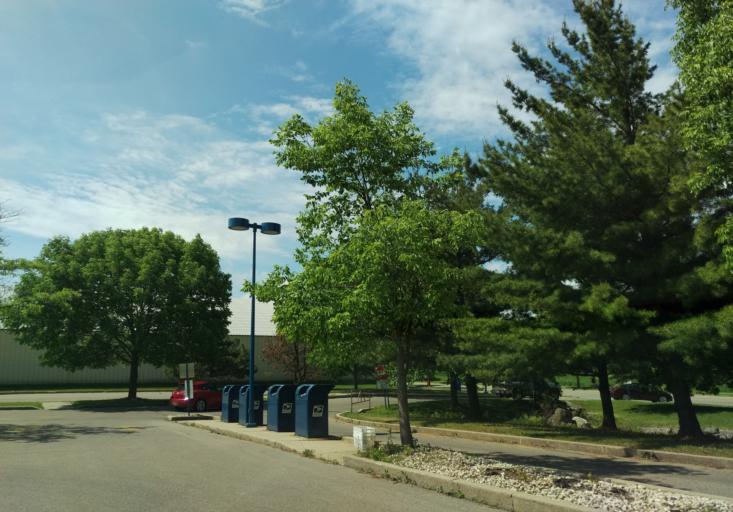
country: US
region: Wisconsin
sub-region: Dane County
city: Middleton
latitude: 43.0487
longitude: -89.4957
